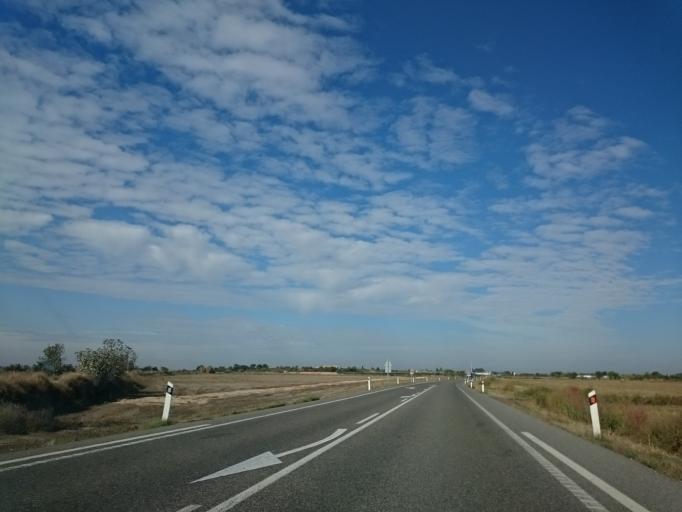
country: ES
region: Catalonia
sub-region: Provincia de Lleida
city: Juneda
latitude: 41.5554
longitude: 0.8075
